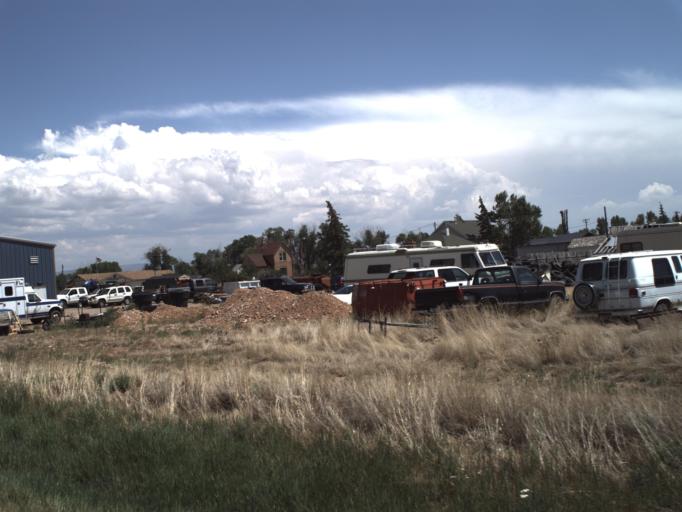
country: US
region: Utah
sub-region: Rich County
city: Randolph
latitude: 41.5241
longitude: -111.1684
